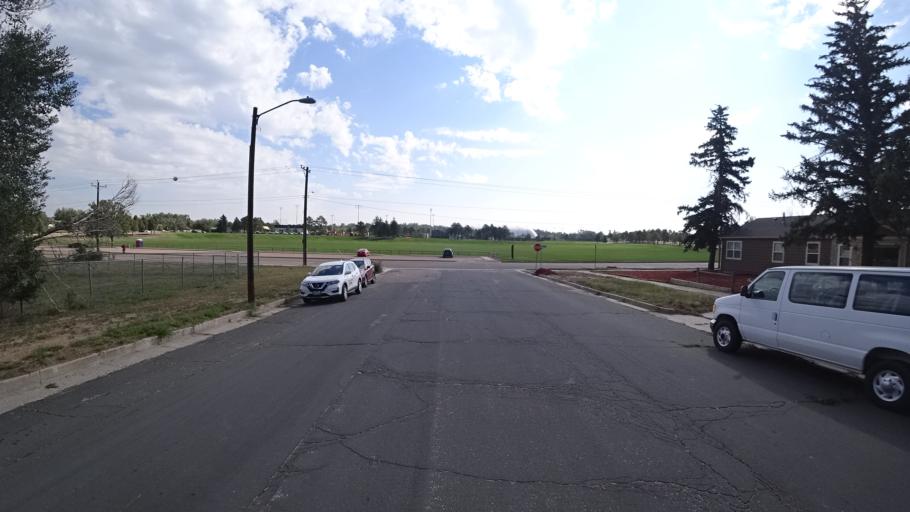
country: US
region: Colorado
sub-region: El Paso County
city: Colorado Springs
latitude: 38.8306
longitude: -104.8044
